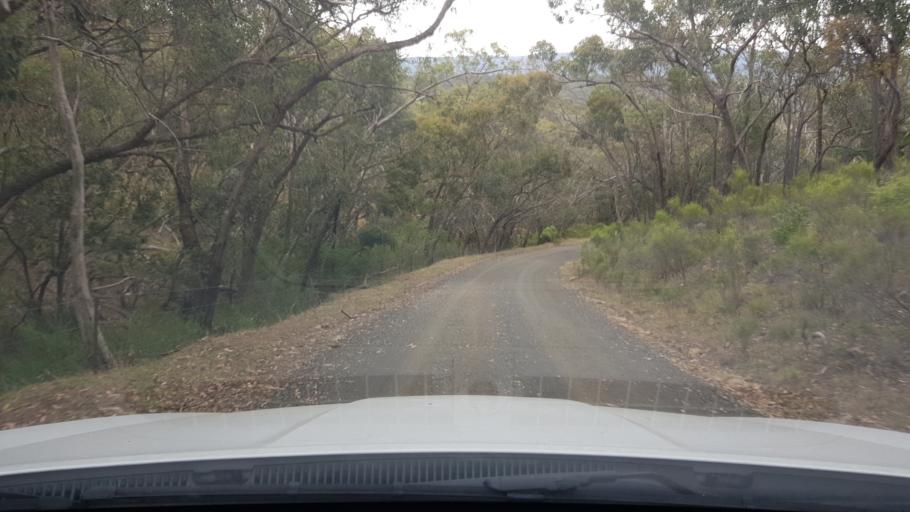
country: AU
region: Victoria
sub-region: Whittlesea
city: Whittlesea
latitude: -37.4892
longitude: 145.0522
